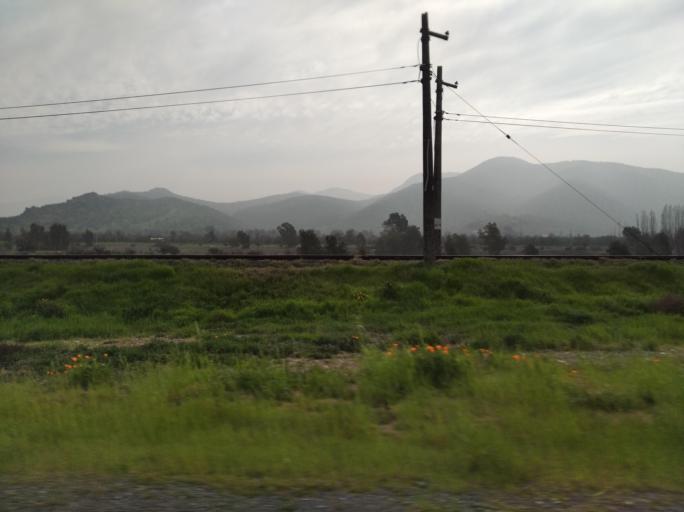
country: CL
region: Santiago Metropolitan
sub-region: Provincia de Chacabuco
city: Lampa
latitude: -33.1509
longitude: -70.9083
